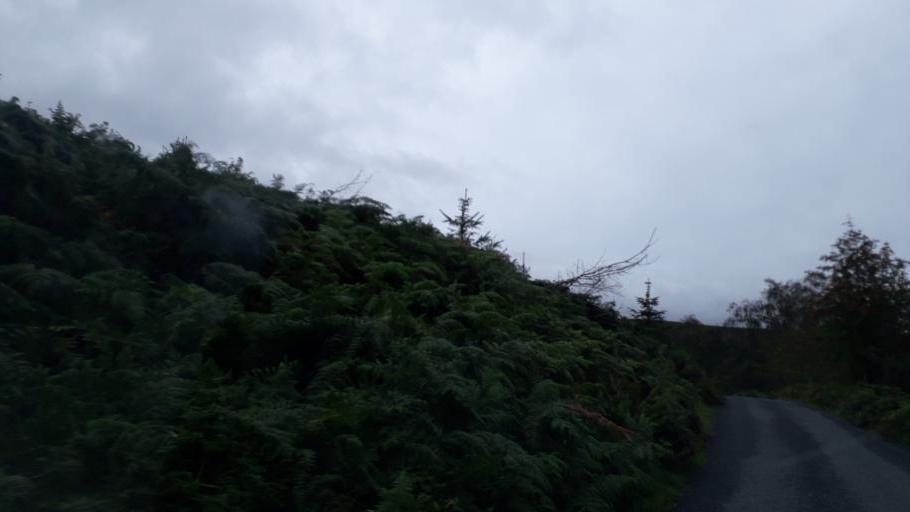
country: IE
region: Leinster
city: Ballinteer
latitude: 53.1839
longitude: -6.2789
